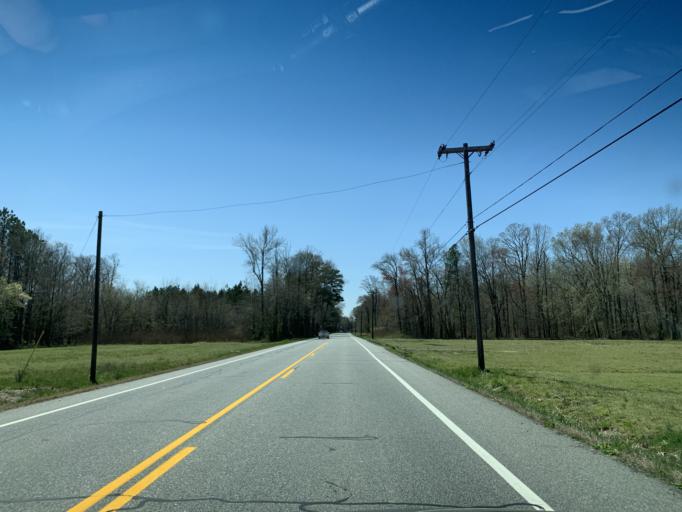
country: US
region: Maryland
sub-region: Talbot County
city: Easton
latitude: 38.8230
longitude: -76.0403
